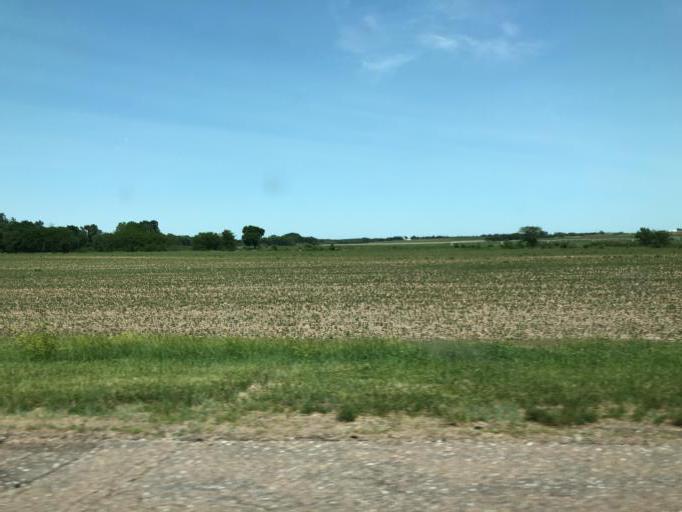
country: US
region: Nebraska
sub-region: Thayer County
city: Hebron
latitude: 40.1508
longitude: -97.5706
